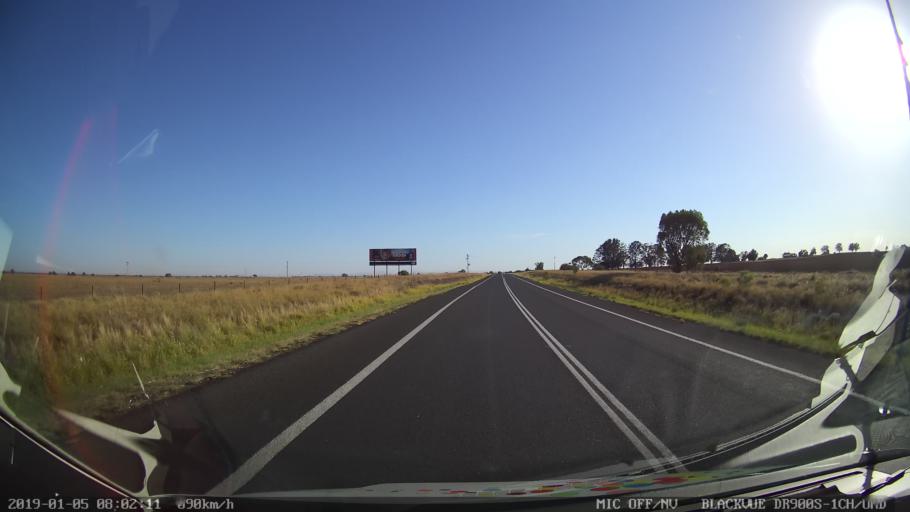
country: AU
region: New South Wales
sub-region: Gilgandra
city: Gilgandra
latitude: -31.6783
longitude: 148.7087
